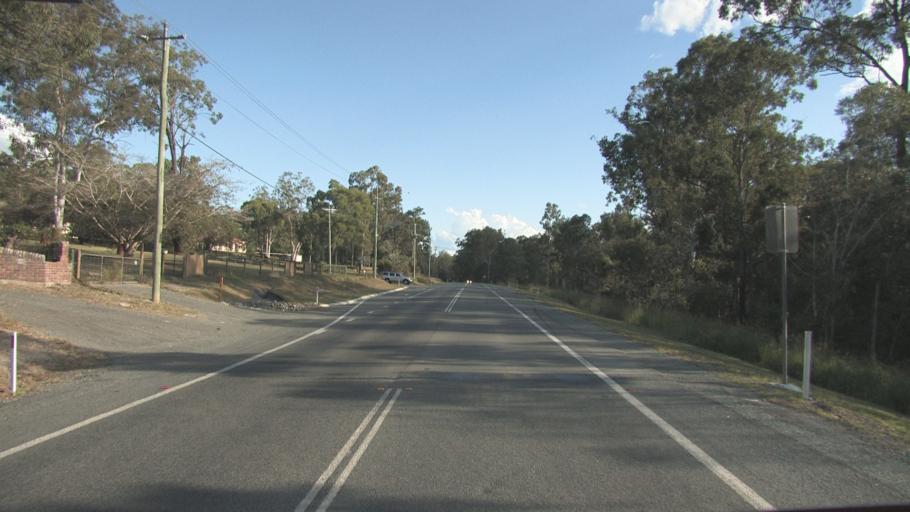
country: AU
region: Queensland
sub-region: Ipswich
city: Springfield Lakes
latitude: -27.7236
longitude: 152.9587
